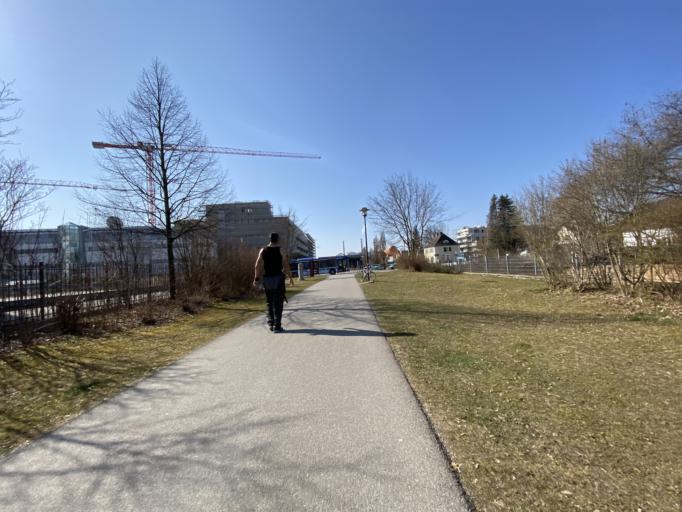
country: DE
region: Bavaria
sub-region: Upper Bavaria
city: Unterfoehring
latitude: 48.1919
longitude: 11.6479
